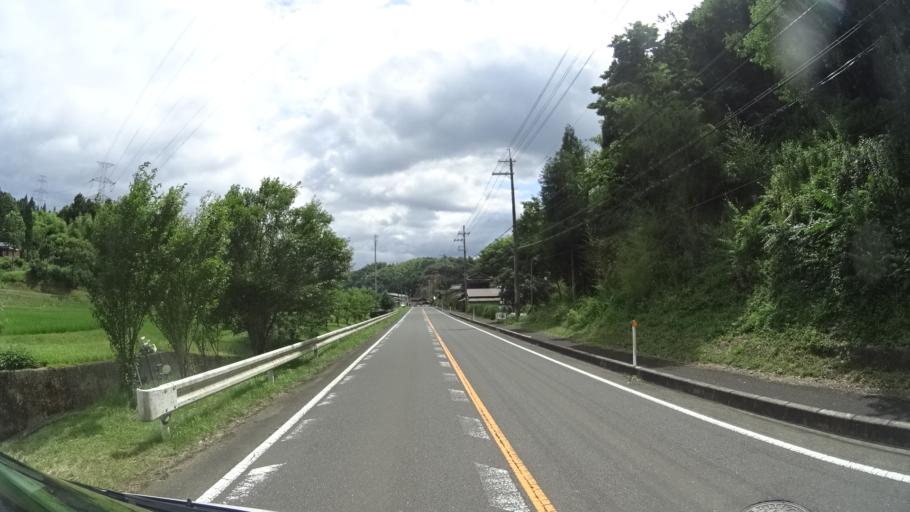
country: JP
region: Kyoto
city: Ayabe
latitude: 35.3379
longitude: 135.2703
